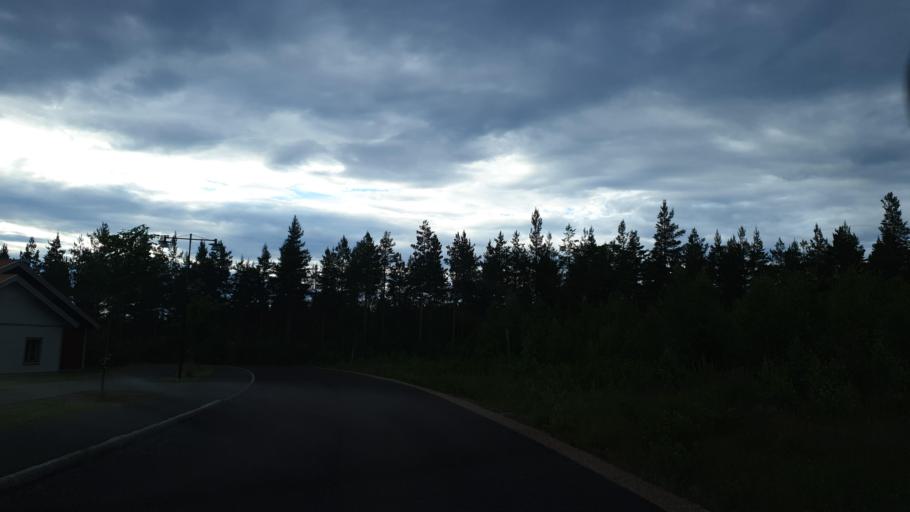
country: SE
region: Dalarna
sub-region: Mora Kommun
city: Mora
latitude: 61.0217
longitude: 14.5865
